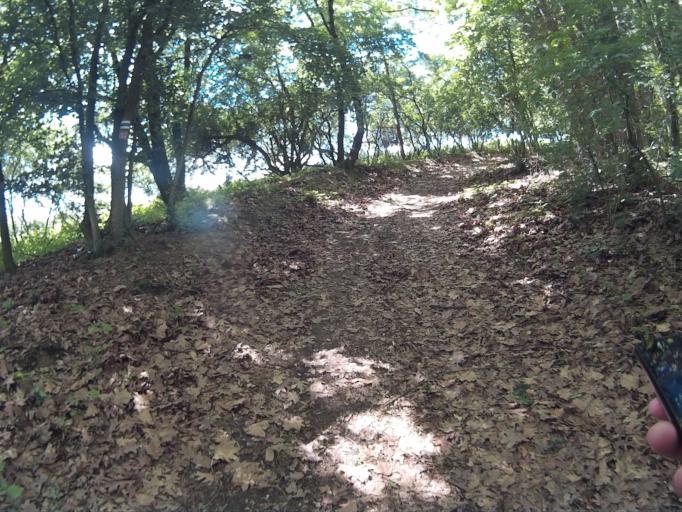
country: HU
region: Vas
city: Kormend
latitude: 46.9644
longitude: 16.5507
